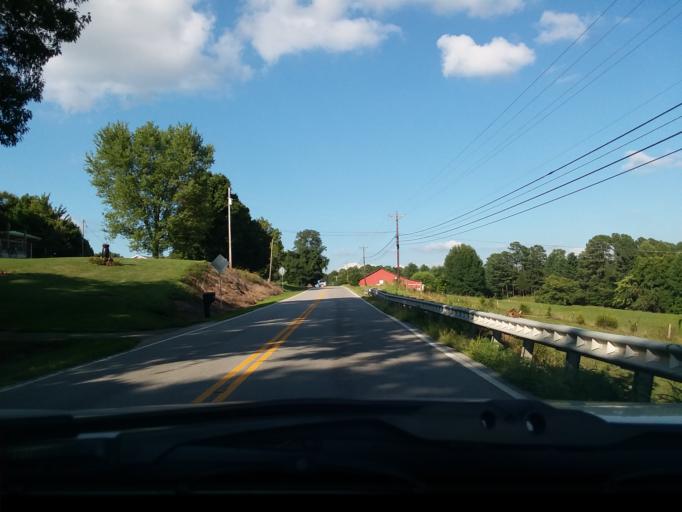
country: US
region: Tennessee
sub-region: Clay County
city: Celina
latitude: 36.5933
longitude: -85.5911
